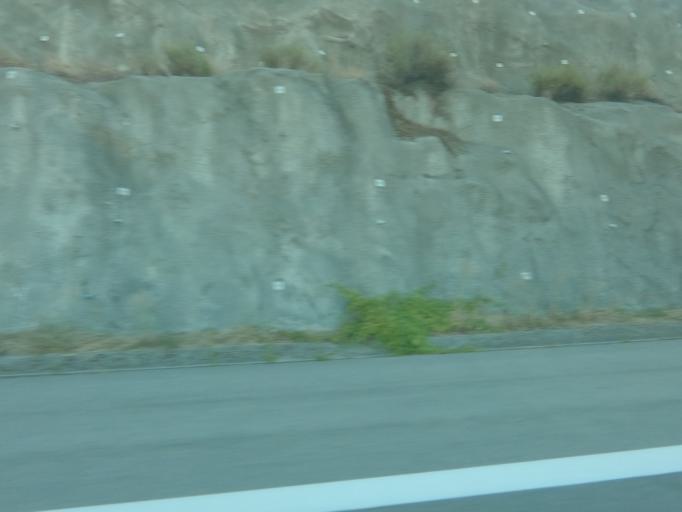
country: PT
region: Vila Real
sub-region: Peso da Regua
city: Peso da Regua
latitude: 41.1780
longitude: -7.7509
